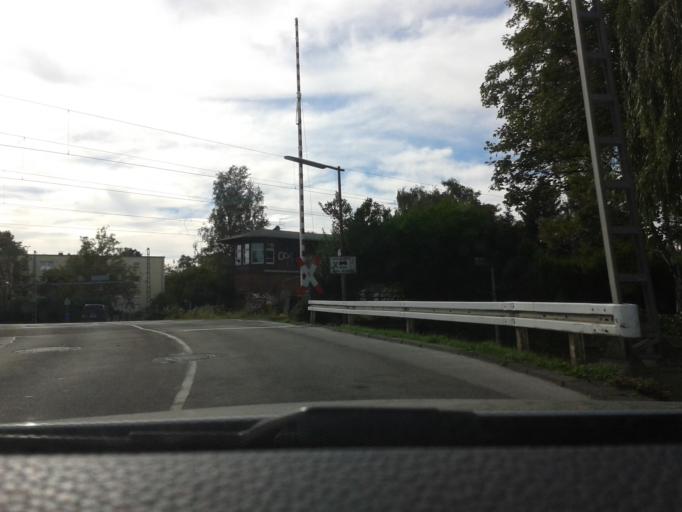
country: DE
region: North Rhine-Westphalia
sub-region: Regierungsbezirk Dusseldorf
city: Muelheim (Ruhr)
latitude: 51.4255
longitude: 6.8444
